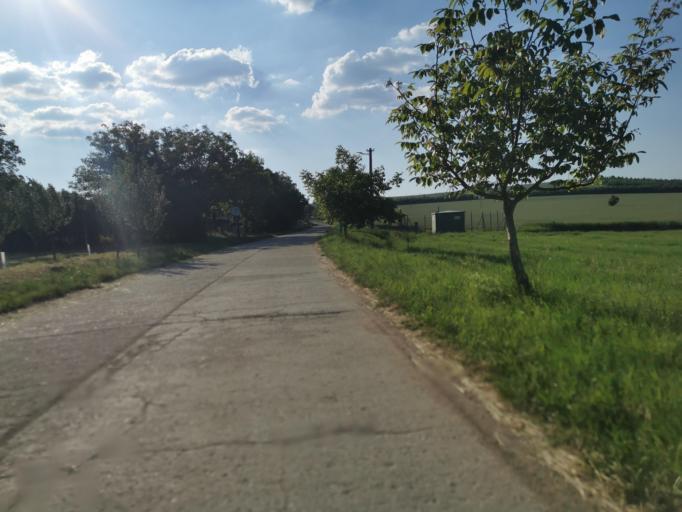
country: CZ
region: South Moravian
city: Straznice
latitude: 48.8804
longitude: 17.3531
